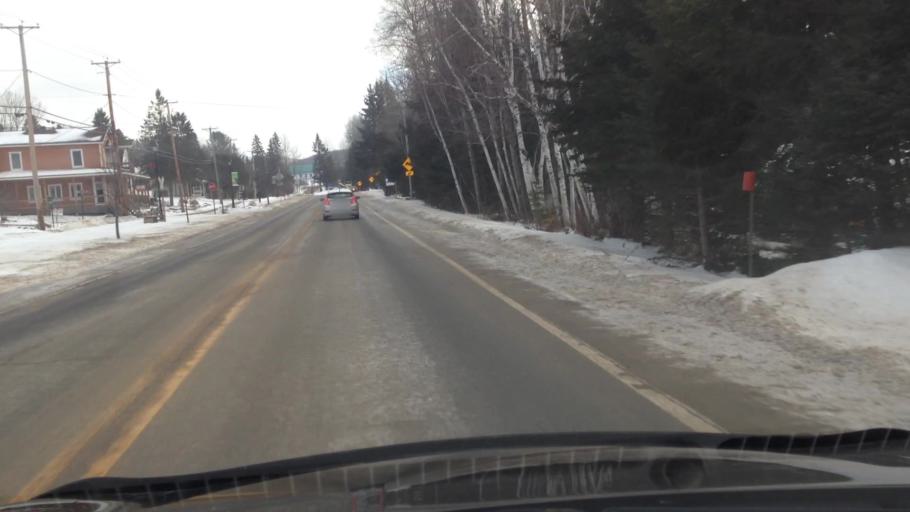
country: CA
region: Quebec
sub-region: Laurentides
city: Mont-Tremblant
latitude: 45.9448
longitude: -74.5488
